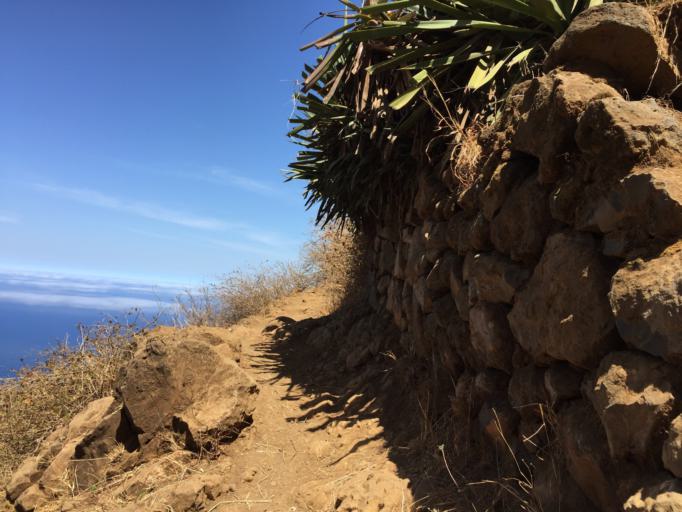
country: CV
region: Mosteiros
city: Porto dos Mosteiros
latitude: 15.0079
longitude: -24.3902
